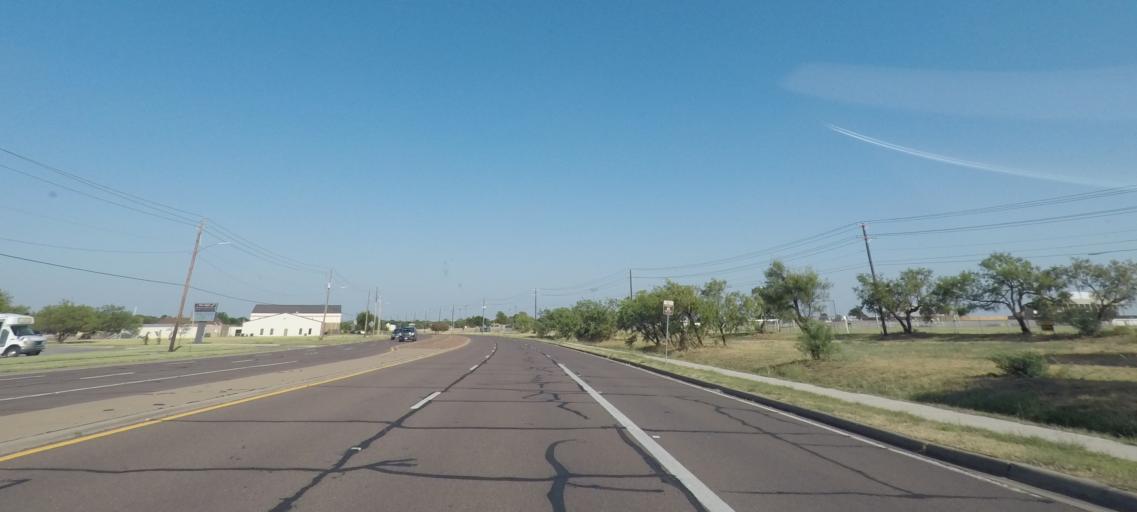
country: US
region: Texas
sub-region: Wichita County
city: Wichita Falls
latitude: 33.8585
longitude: -98.5859
